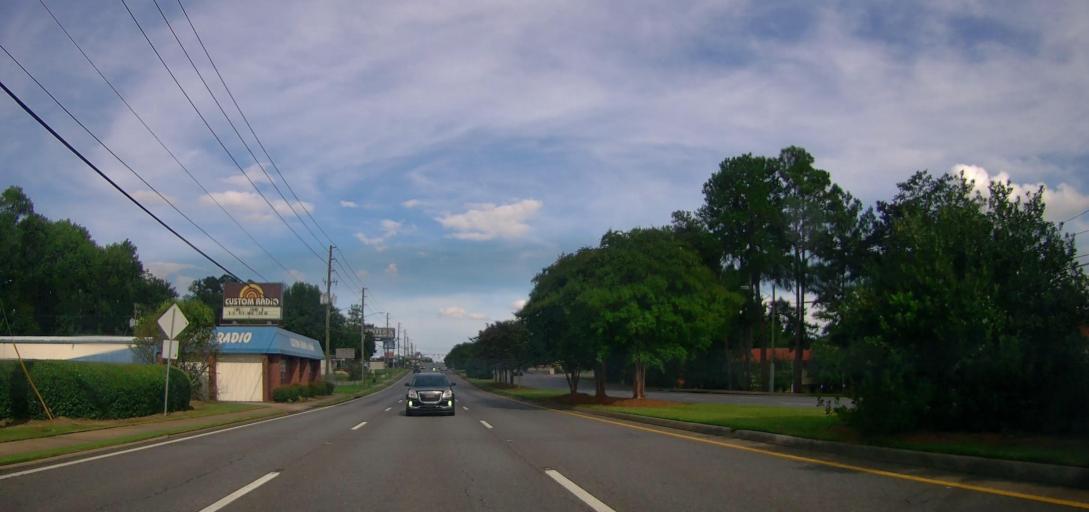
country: US
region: Georgia
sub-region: Muscogee County
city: Columbus
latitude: 32.5072
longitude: -84.9596
